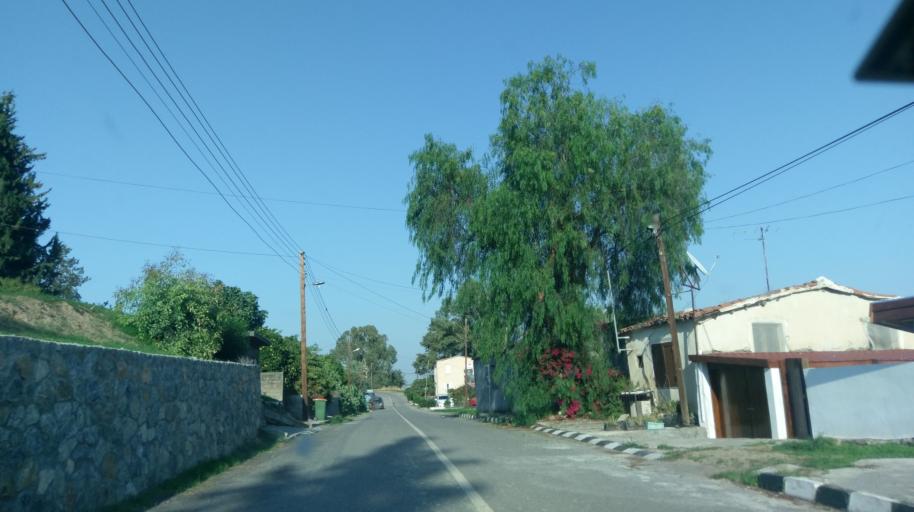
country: CY
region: Lefkosia
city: Lefka
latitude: 35.0913
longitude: 32.8432
